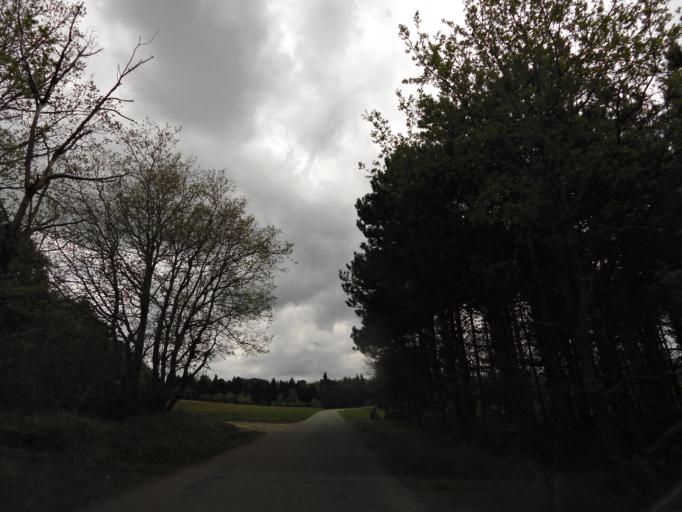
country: FR
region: Languedoc-Roussillon
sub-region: Departement de l'Aude
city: Saint-Martin-Lalande
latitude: 43.3459
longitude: 2.0618
